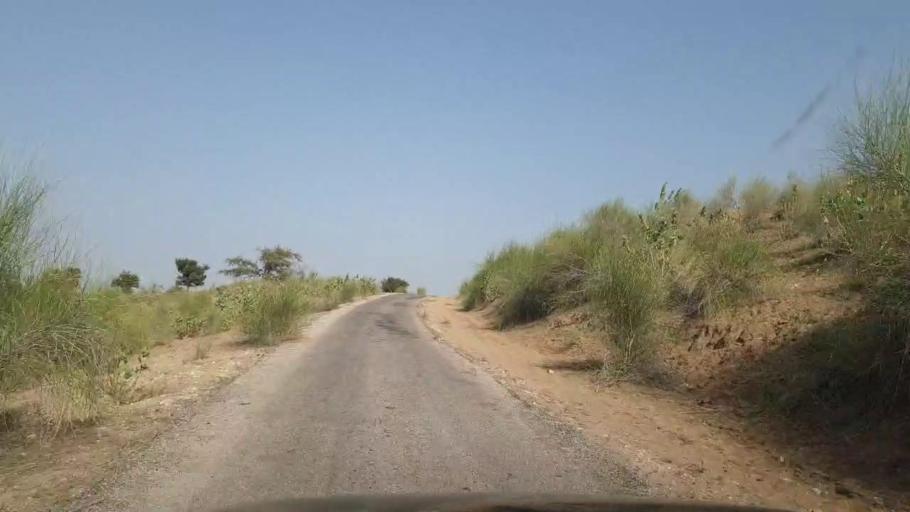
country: PK
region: Sindh
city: Islamkot
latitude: 25.1144
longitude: 70.4322
